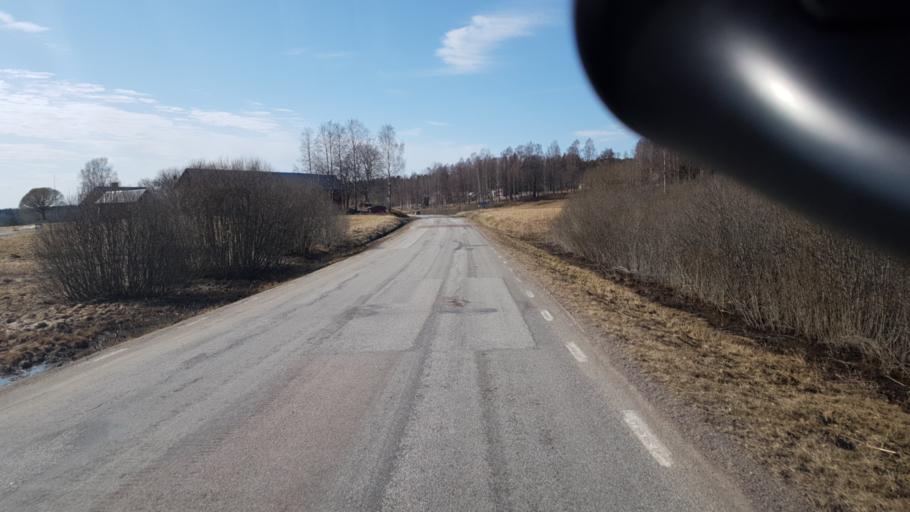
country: SE
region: Vaermland
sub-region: Arvika Kommun
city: Arvika
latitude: 59.6600
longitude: 12.7156
